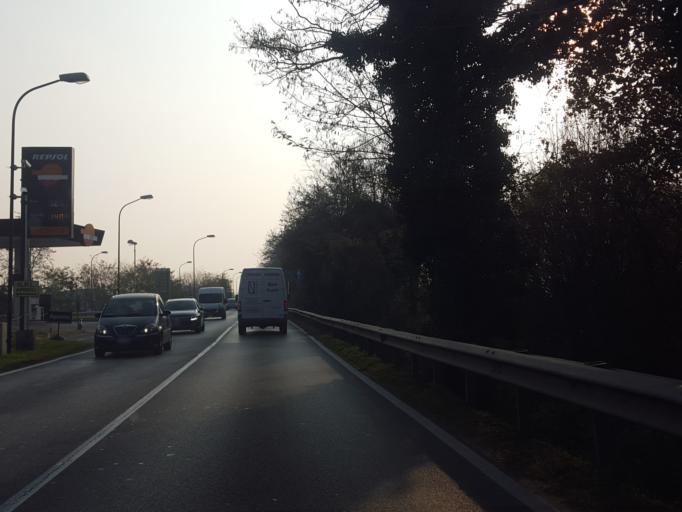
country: IT
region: Veneto
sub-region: Provincia di Treviso
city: Treviso
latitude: 45.6660
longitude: 12.2224
